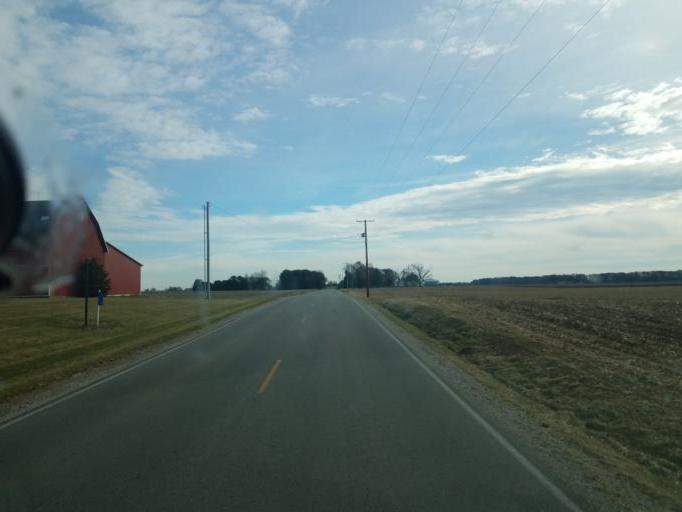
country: US
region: Ohio
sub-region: Crawford County
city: Bucyrus
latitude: 40.7191
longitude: -82.9136
